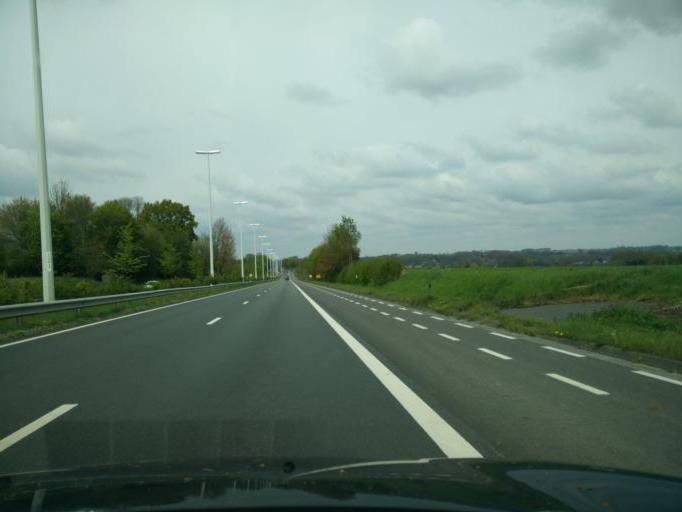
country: BE
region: Flanders
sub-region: Provincie Oost-Vlaanderen
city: Oudenaarde
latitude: 50.8058
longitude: 3.5972
